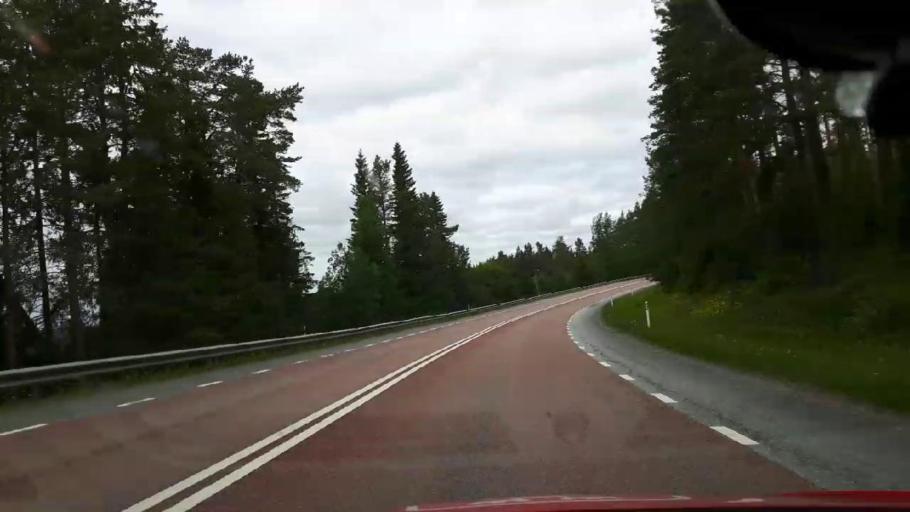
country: SE
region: Jaemtland
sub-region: Braecke Kommun
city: Braecke
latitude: 62.8912
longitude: 15.2638
